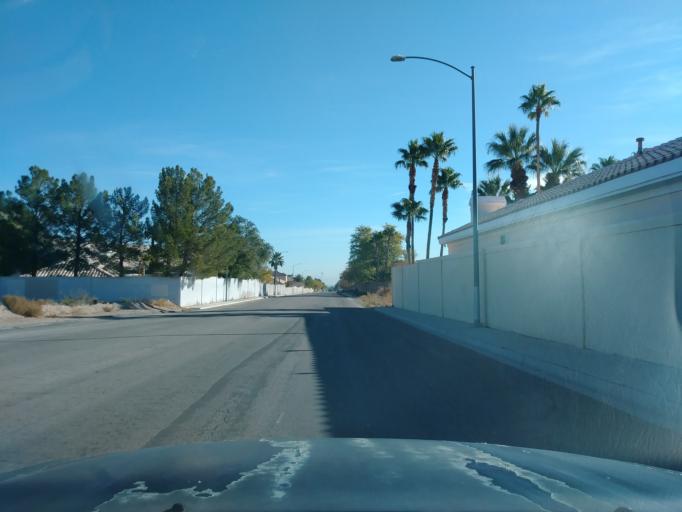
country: US
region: Nevada
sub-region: Clark County
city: Spring Valley
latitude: 36.1477
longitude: -115.2765
